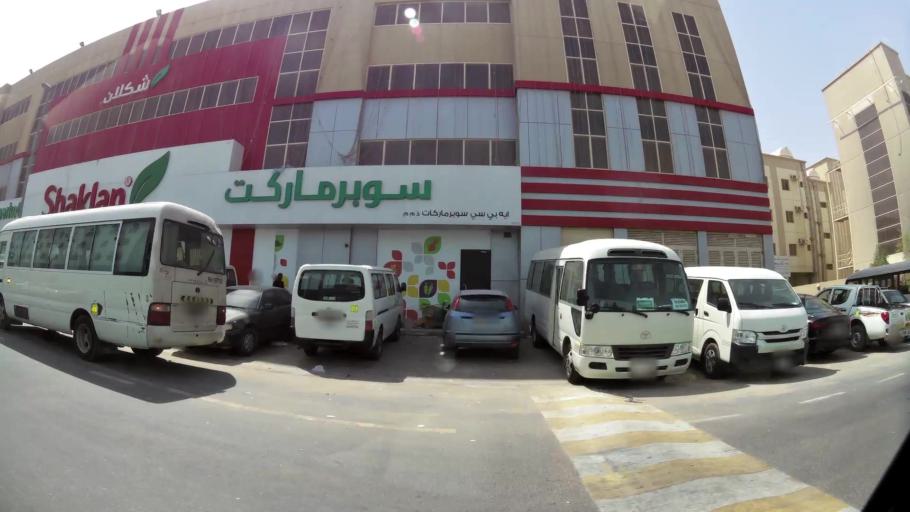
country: AE
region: Dubai
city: Dubai
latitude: 25.1574
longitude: 55.2482
